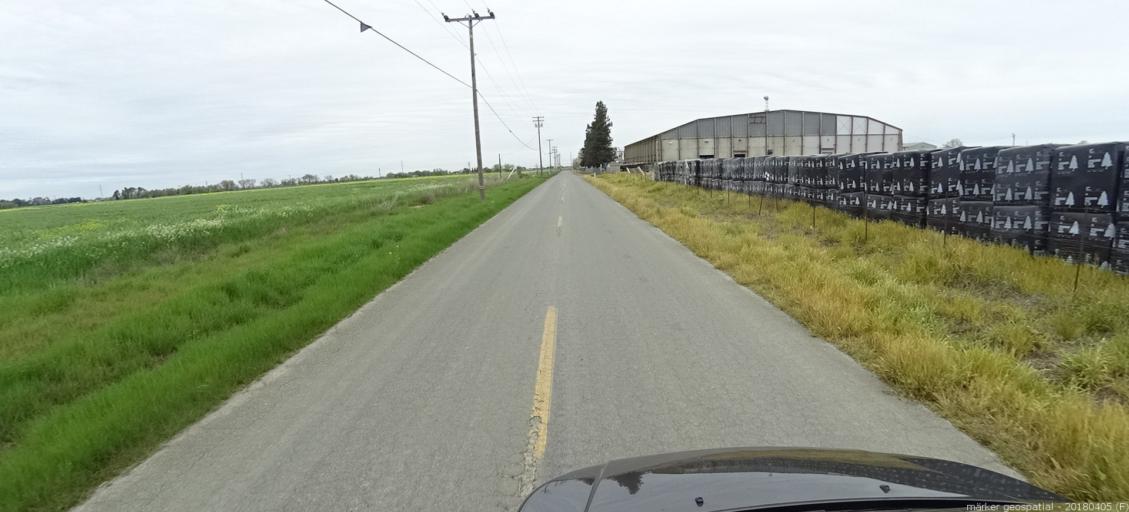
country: US
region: California
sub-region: Sacramento County
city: Elk Grove
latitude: 38.3458
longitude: -121.3990
